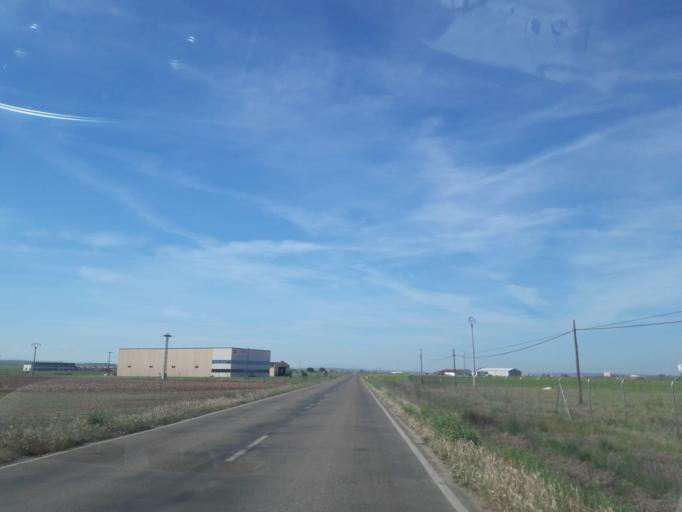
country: ES
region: Castille and Leon
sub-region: Provincia de Salamanca
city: Villoruela
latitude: 40.9893
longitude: -5.4055
